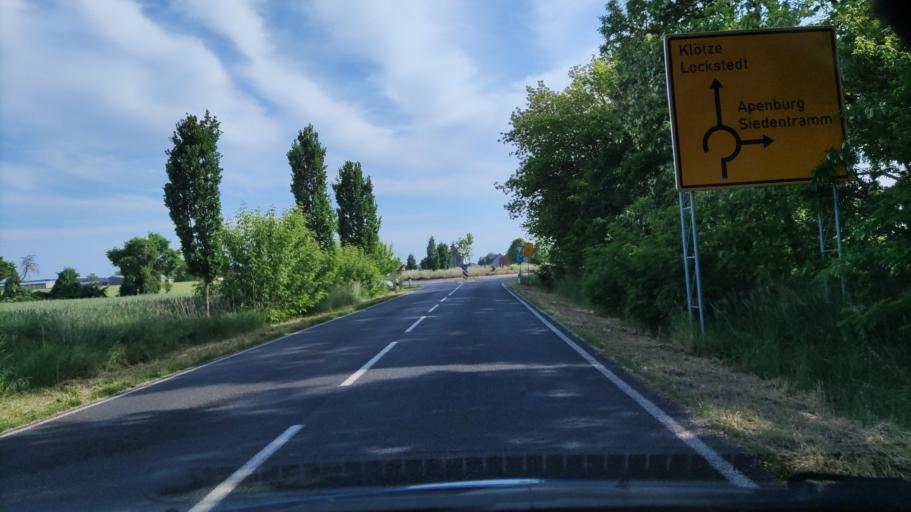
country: DE
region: Saxony-Anhalt
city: Klotze
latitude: 52.6698
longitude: 11.2043
